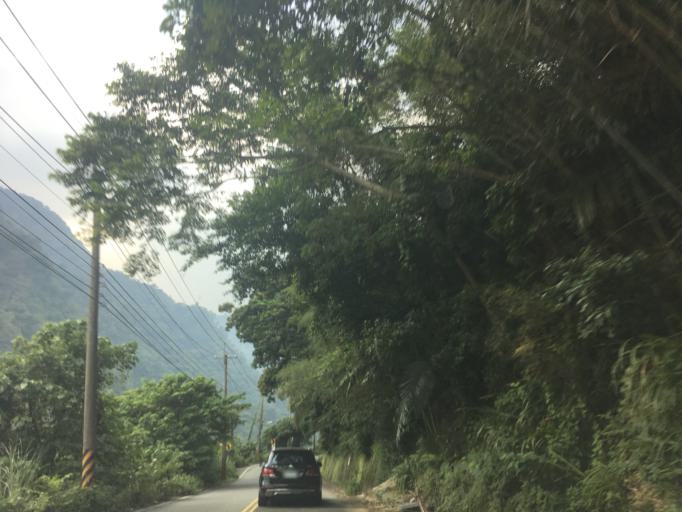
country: TW
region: Taiwan
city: Fengyuan
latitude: 24.3116
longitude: 120.9223
